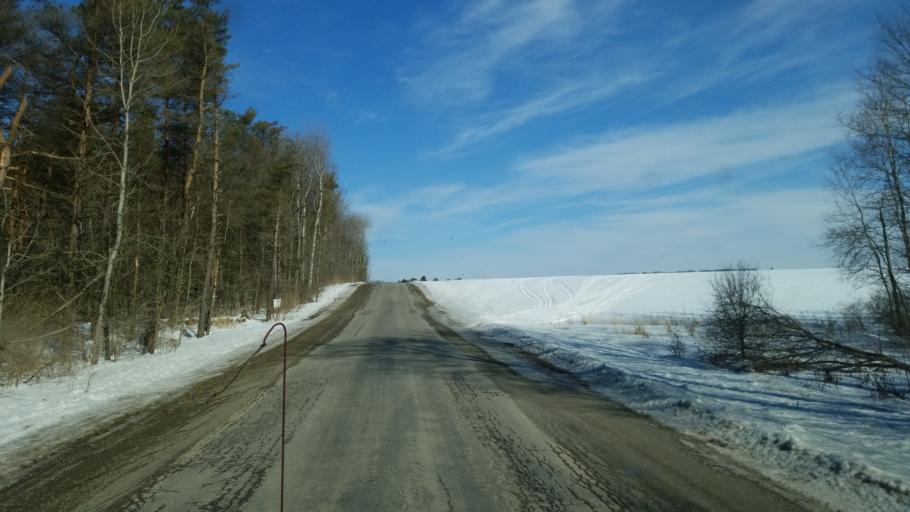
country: US
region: New York
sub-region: Allegany County
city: Andover
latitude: 42.0741
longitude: -77.7718
